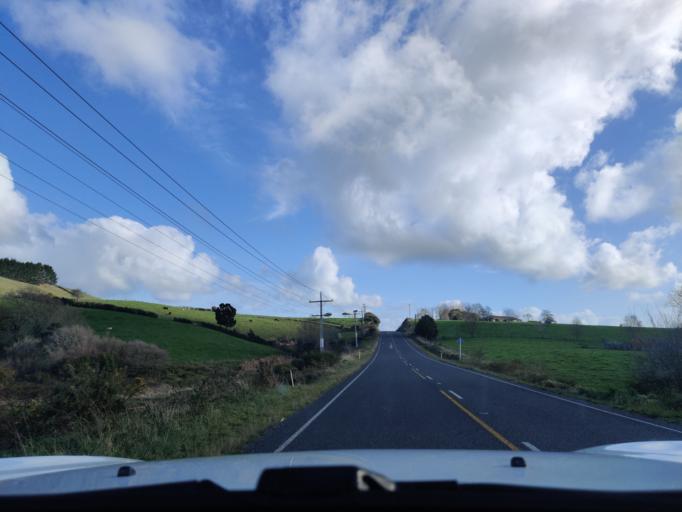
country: NZ
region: Waikato
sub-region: Waikato District
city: Te Kauwhata
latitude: -37.3687
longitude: 175.2438
